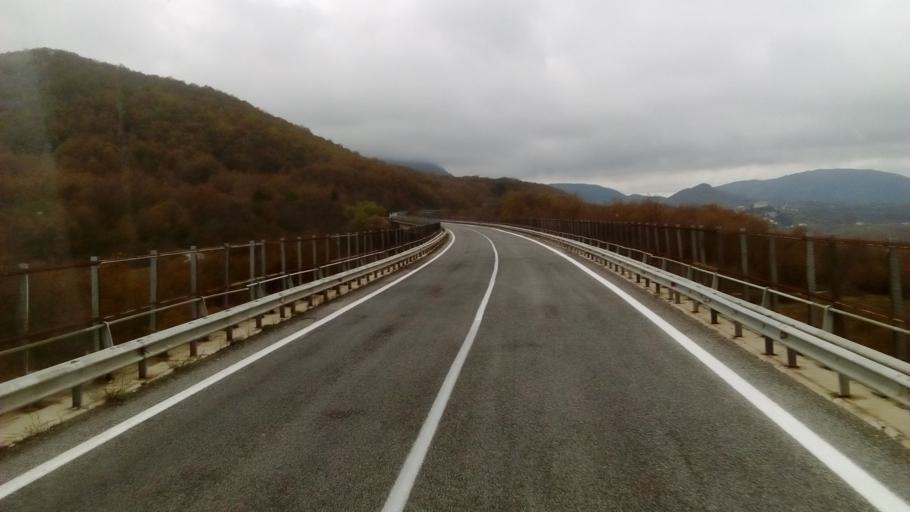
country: IT
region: Molise
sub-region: Provincia di Isernia
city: Chiauci
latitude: 41.6725
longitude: 14.3702
